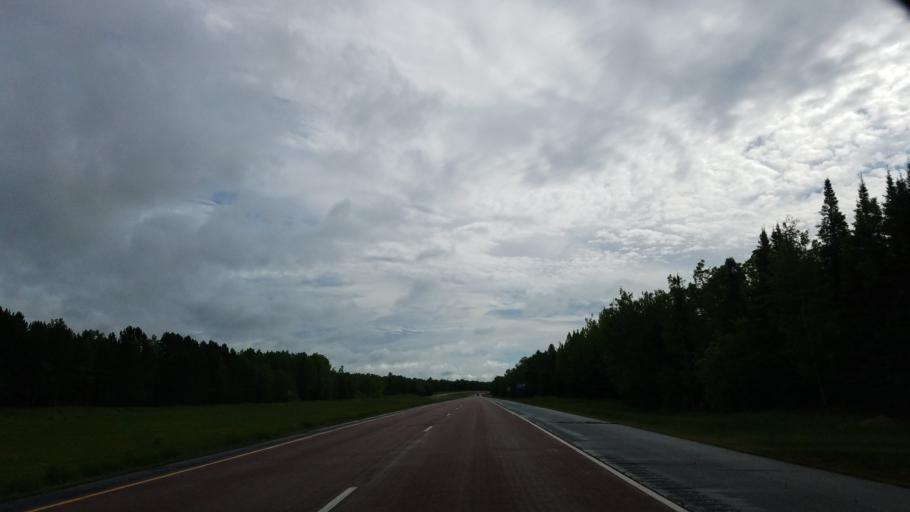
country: US
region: Minnesota
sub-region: Lake County
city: Two Harbors
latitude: 46.9214
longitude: -91.8639
